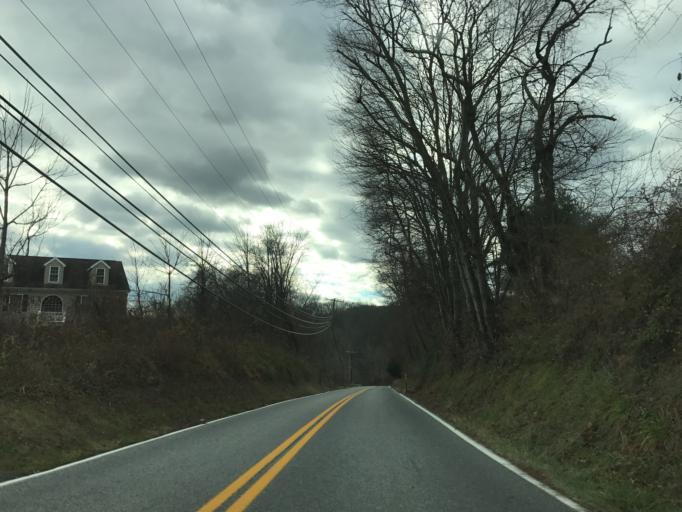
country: US
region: Pennsylvania
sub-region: York County
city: New Freedom
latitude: 39.6322
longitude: -76.6334
